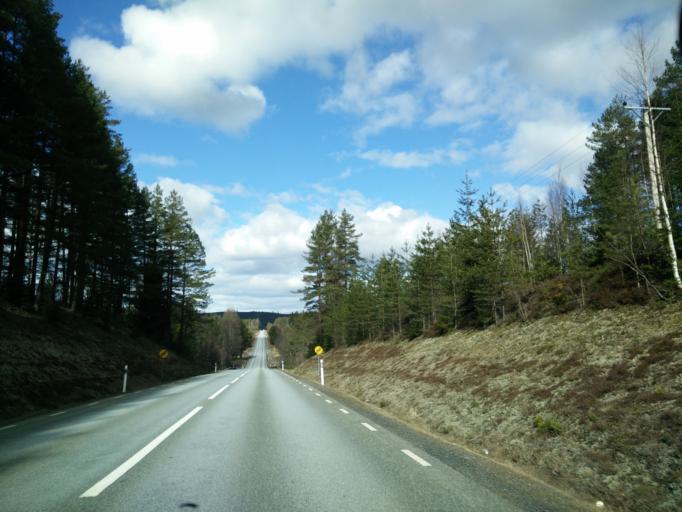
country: SE
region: Vaermland
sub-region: Munkfors Kommun
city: Munkfors
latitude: 59.9298
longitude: 13.5761
